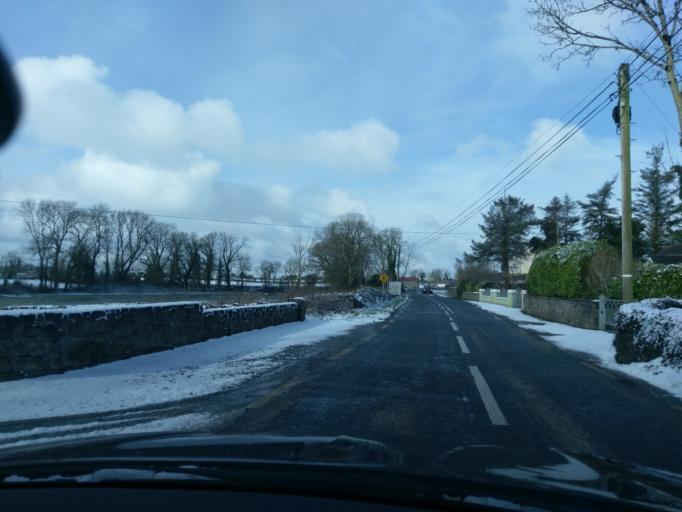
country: IE
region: Connaught
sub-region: County Galway
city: Athenry
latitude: 53.2023
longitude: -8.7610
